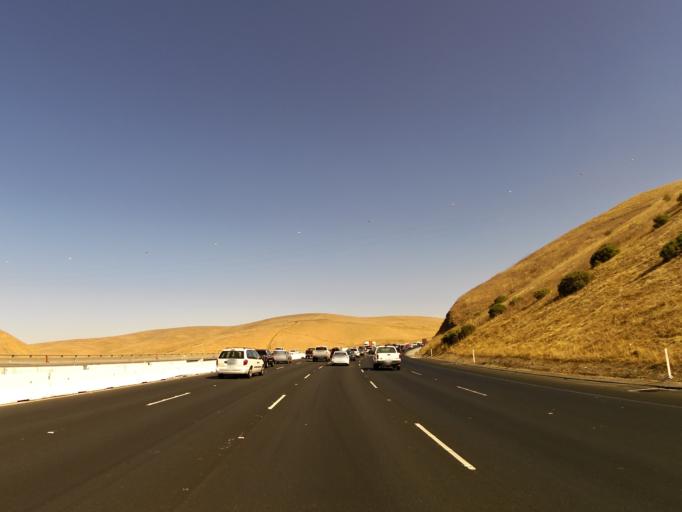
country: US
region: California
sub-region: Alameda County
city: Livermore
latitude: 37.7217
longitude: -121.6819
